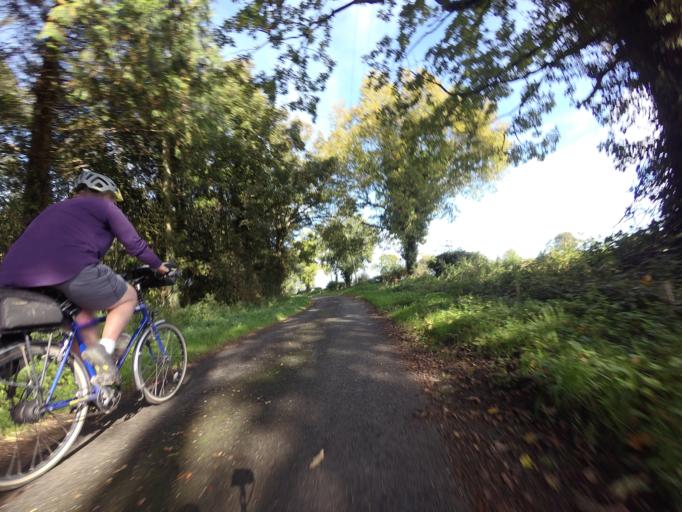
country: GB
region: England
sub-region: Norfolk
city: Fakenham
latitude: 52.8899
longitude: 0.6835
